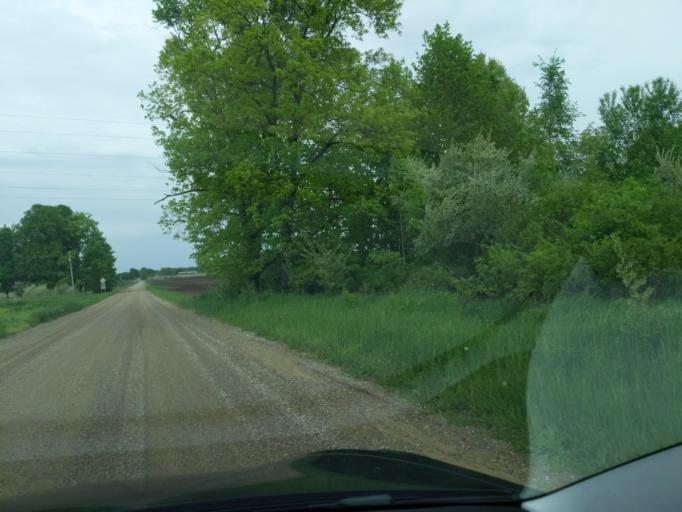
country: US
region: Michigan
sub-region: Ingham County
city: Stockbridge
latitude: 42.4193
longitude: -84.2141
